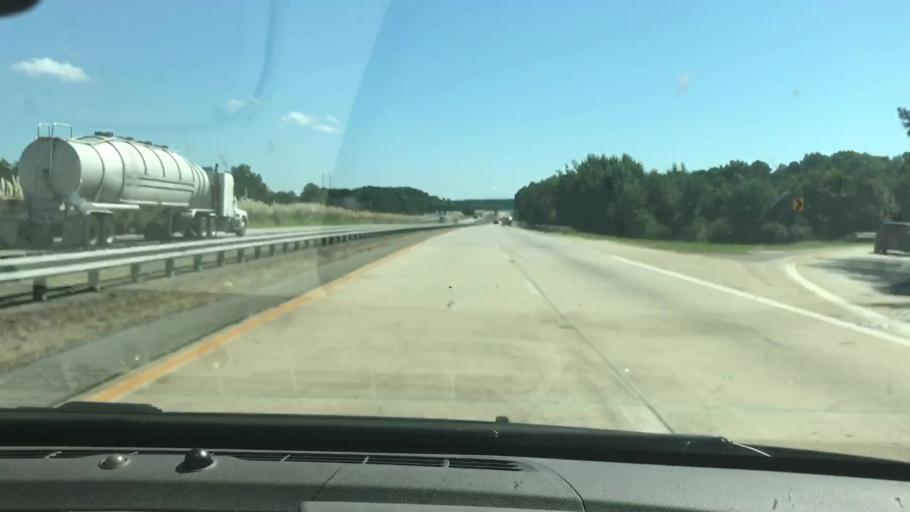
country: US
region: Alabama
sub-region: Russell County
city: Phenix City
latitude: 32.5452
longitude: -84.9596
